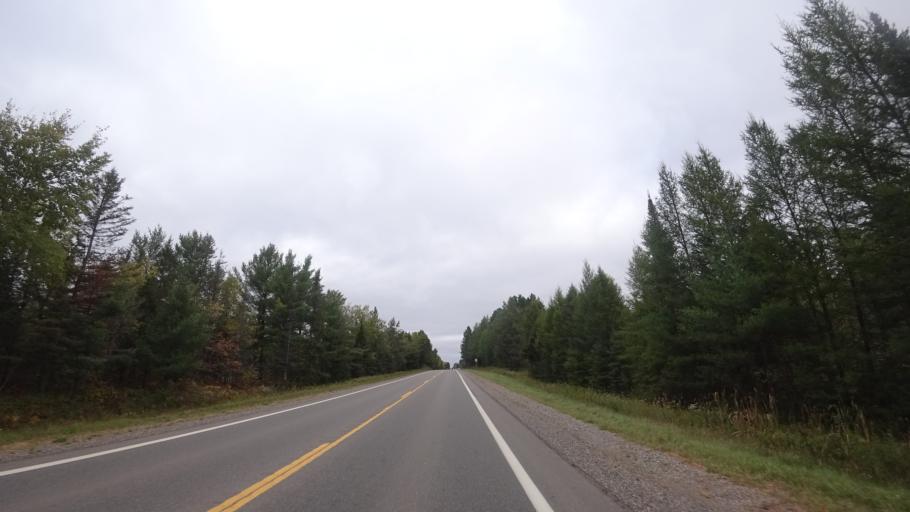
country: US
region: Michigan
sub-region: Iron County
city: Crystal Falls
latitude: 46.1263
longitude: -88.0914
